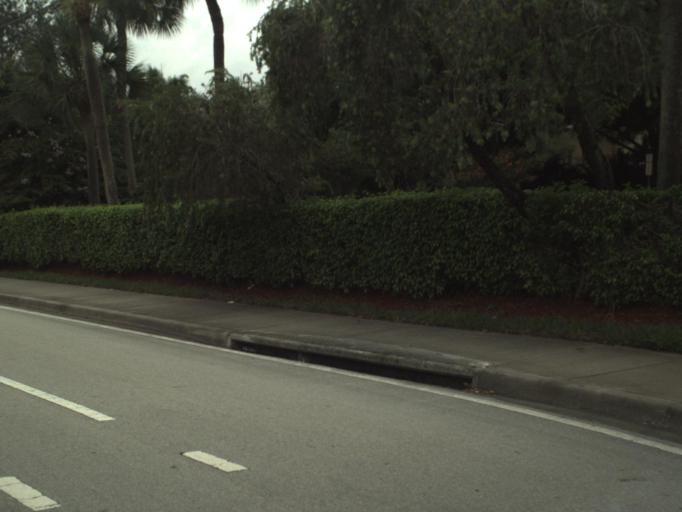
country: US
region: Florida
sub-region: Broward County
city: Pine Island Ridge
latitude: 26.1468
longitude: -80.2848
